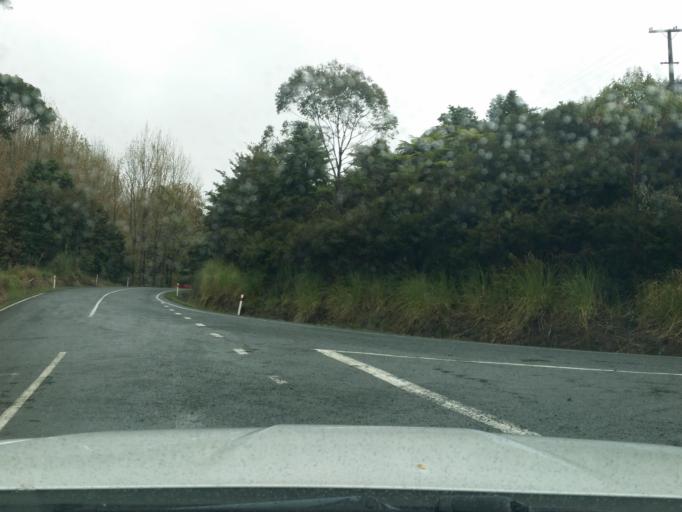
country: NZ
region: Northland
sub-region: Kaipara District
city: Dargaville
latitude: -35.7835
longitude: 173.9608
